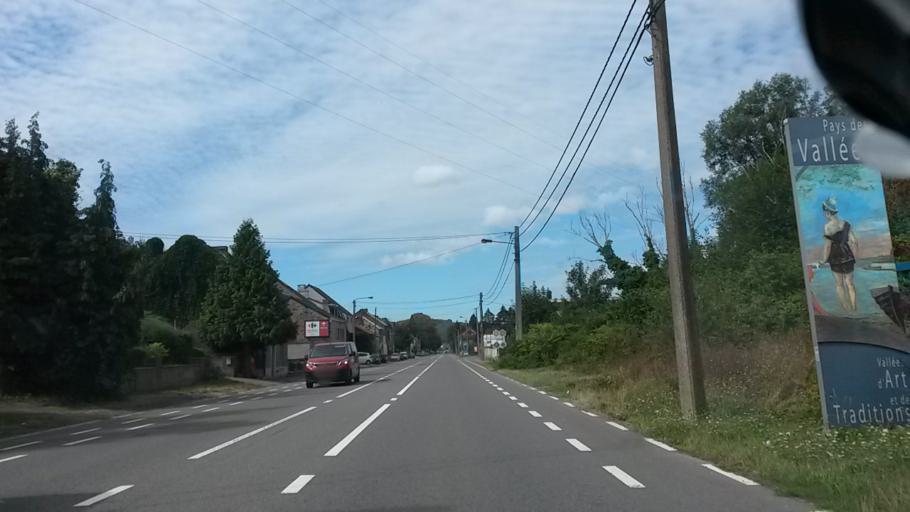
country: BE
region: Wallonia
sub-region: Province de Namur
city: Andenne
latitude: 50.4983
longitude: 5.1252
